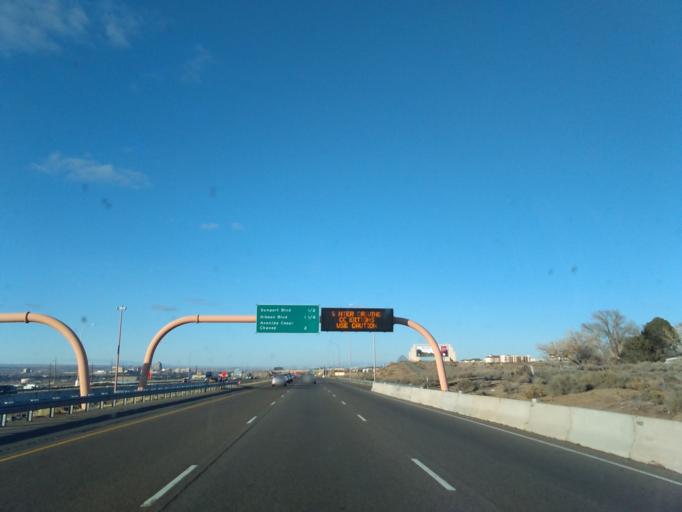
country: US
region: New Mexico
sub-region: Bernalillo County
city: South Valley
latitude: 35.0368
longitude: -106.6379
